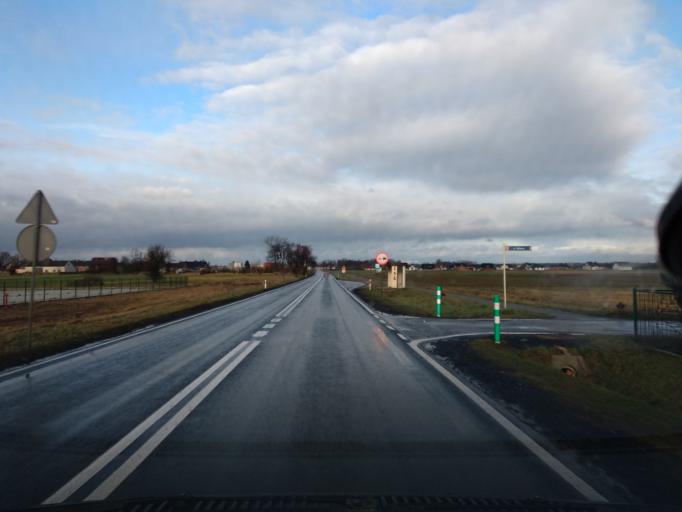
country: PL
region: Greater Poland Voivodeship
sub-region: Powiat koninski
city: Rychwal
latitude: 52.0568
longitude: 18.1634
